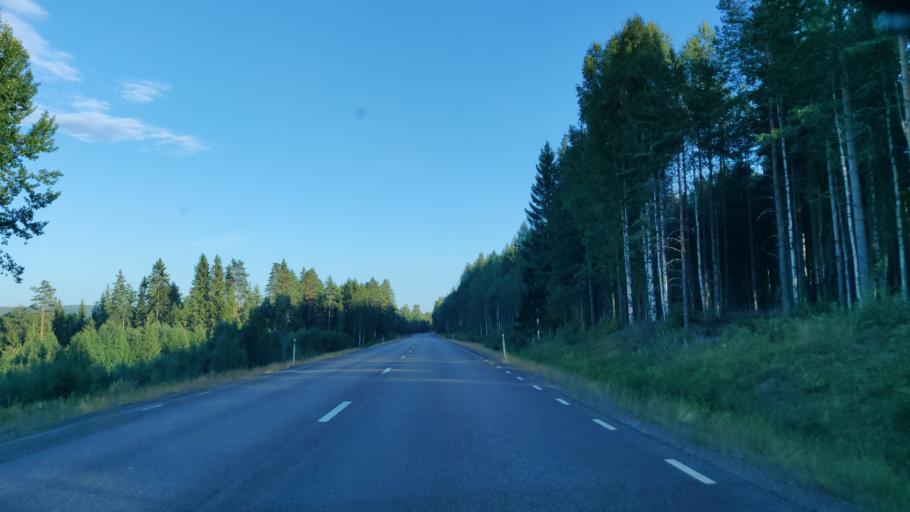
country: SE
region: Vaermland
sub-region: Hagfors Kommun
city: Ekshaerad
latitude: 60.1485
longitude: 13.5207
